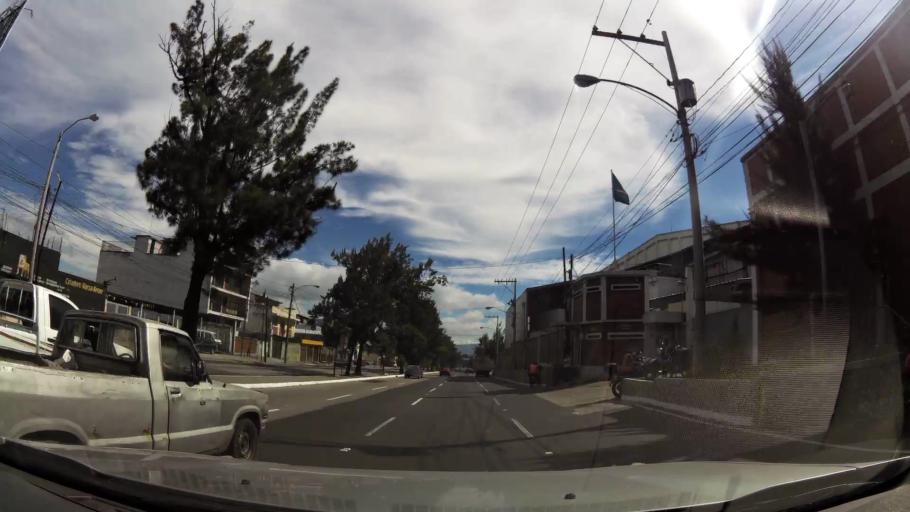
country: GT
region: Guatemala
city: Mixco
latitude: 14.6346
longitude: -90.5606
